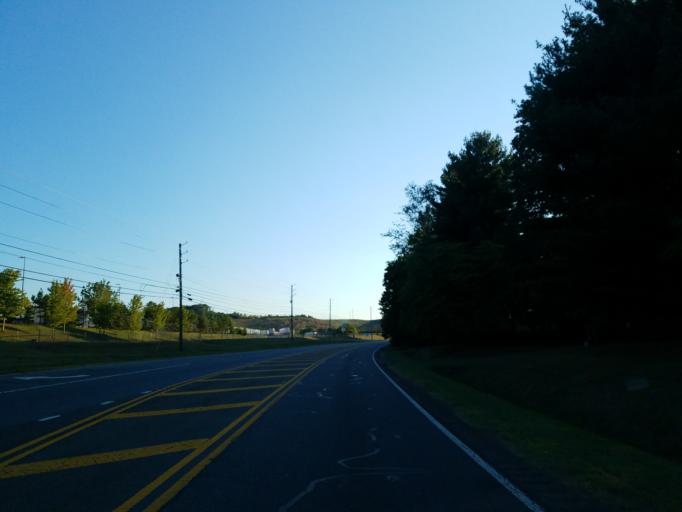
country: US
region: Georgia
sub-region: Bartow County
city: Rydal
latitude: 34.2953
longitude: -84.7334
